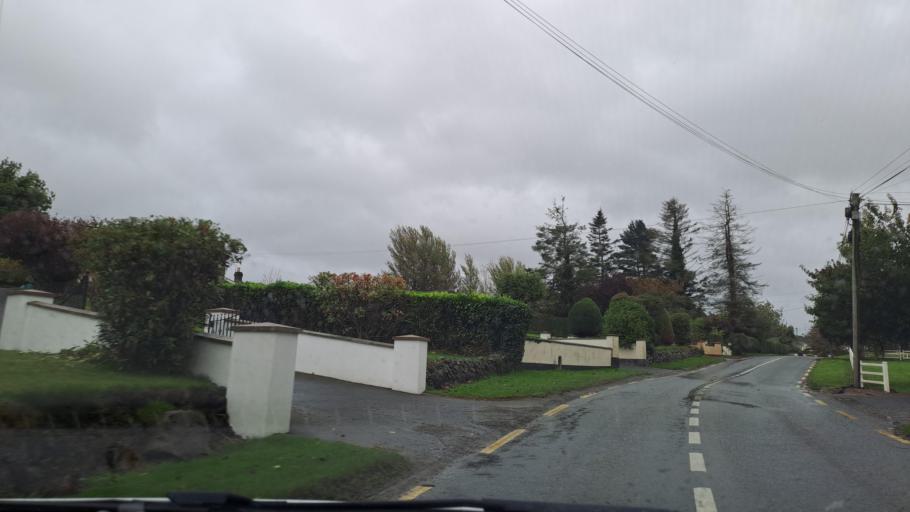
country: IE
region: Leinster
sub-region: Lu
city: Dundalk
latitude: 53.9660
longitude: -6.4705
